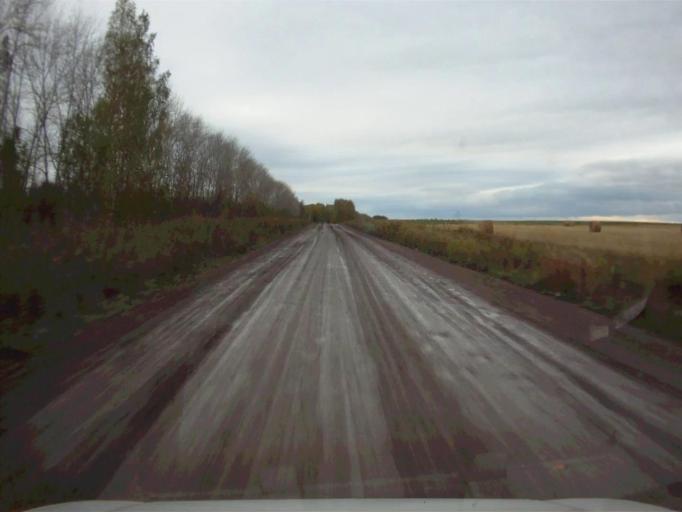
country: RU
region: Sverdlovsk
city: Mikhaylovsk
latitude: 56.1655
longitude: 59.2361
